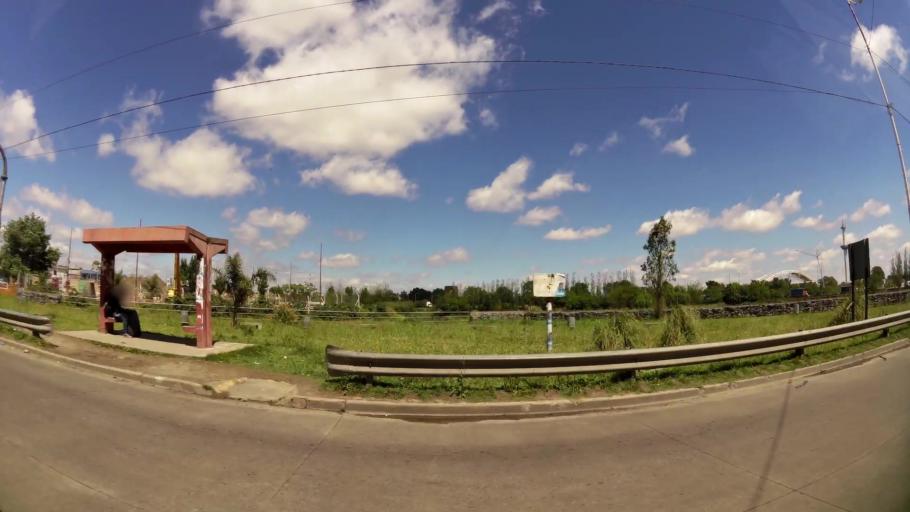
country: AR
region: Buenos Aires F.D.
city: Villa Lugano
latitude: -34.6814
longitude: -58.4389
